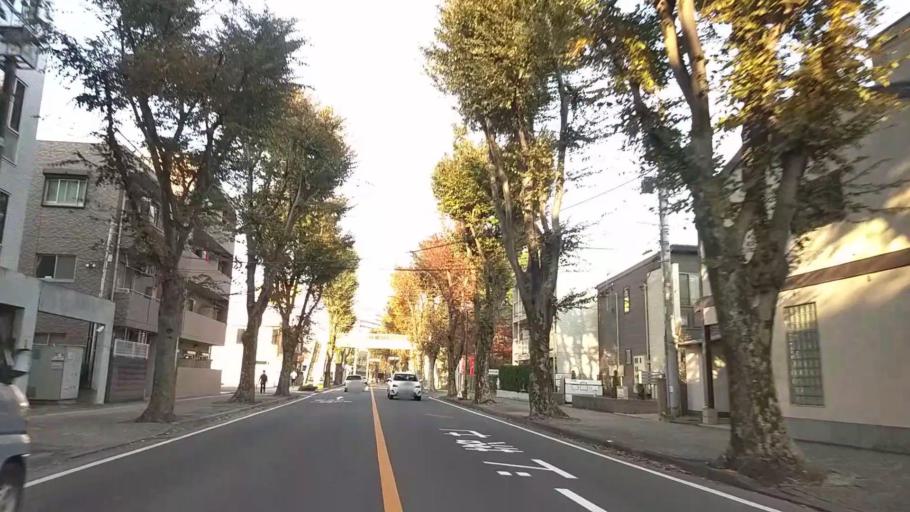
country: JP
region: Saitama
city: Tokorozawa
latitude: 35.8026
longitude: 139.4500
